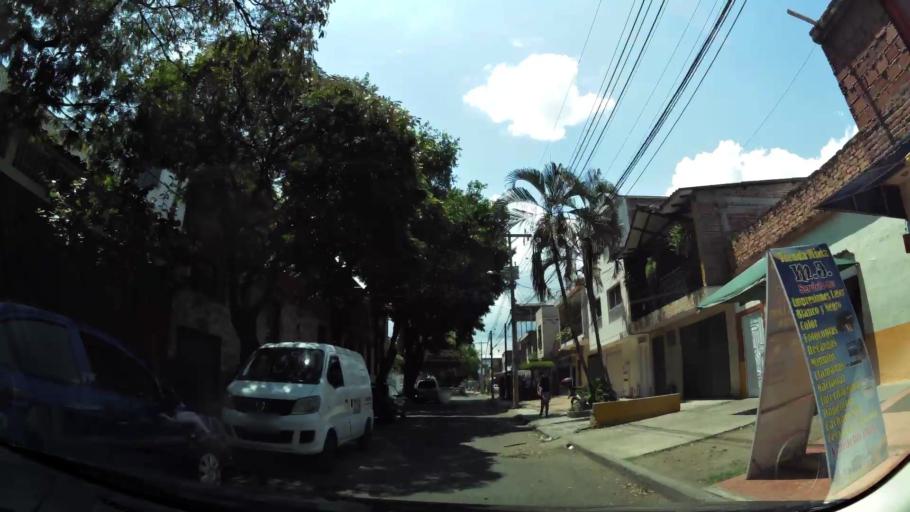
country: CO
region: Valle del Cauca
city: Cali
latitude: 3.4461
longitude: -76.4996
